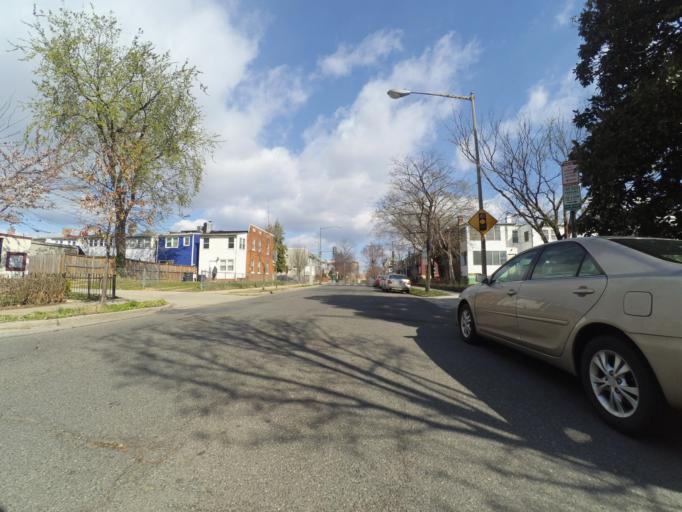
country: US
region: Maryland
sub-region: Prince George's County
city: Silver Hill
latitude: 38.8870
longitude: -76.9790
